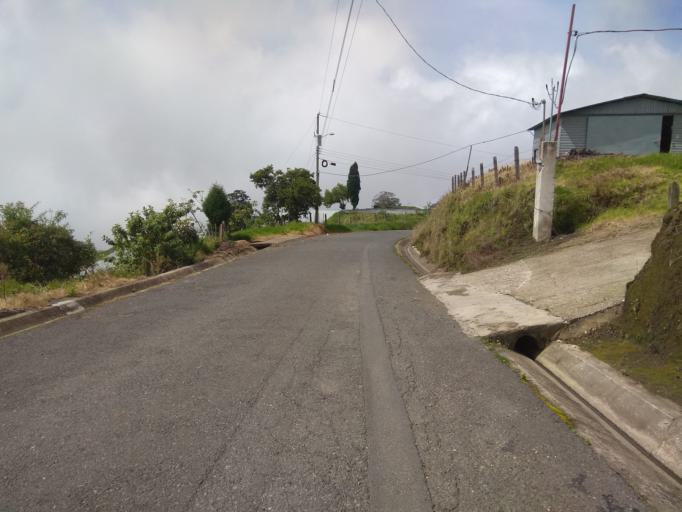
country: CR
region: Cartago
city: Cot
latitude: 9.9485
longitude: -83.9109
